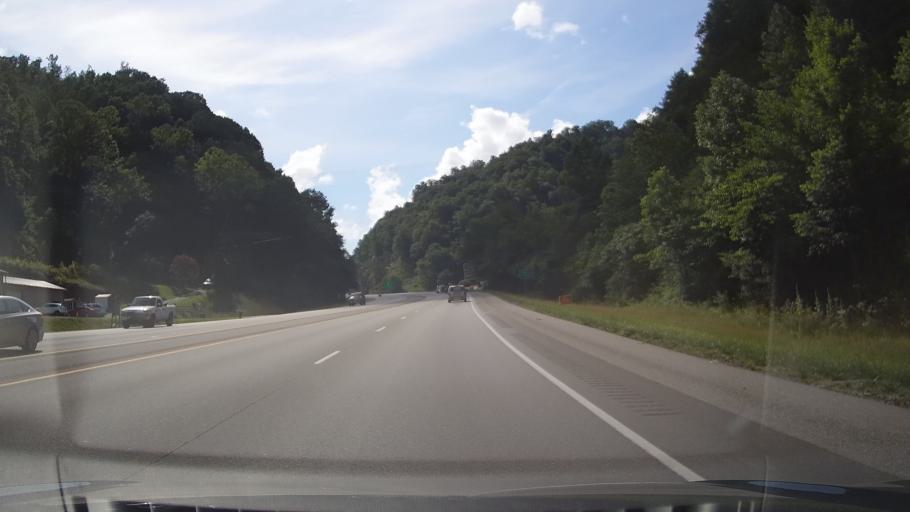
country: US
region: Kentucky
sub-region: Floyd County
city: Prestonsburg
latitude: 37.6428
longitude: -82.7650
